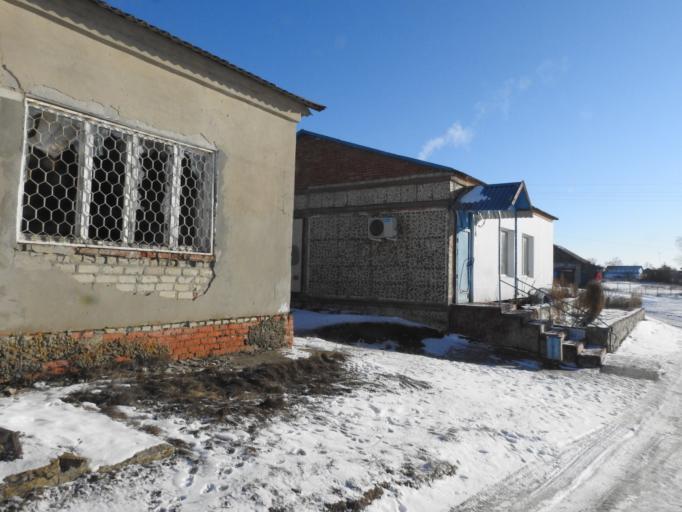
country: RU
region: Saratov
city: Lysyye Gory
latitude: 51.4305
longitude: 44.9333
